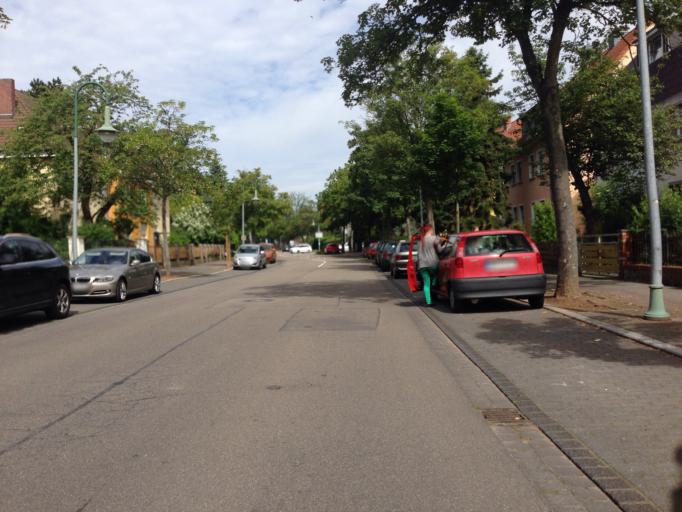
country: DE
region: Hesse
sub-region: Regierungsbezirk Darmstadt
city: Hanau am Main
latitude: 50.1412
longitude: 8.9017
